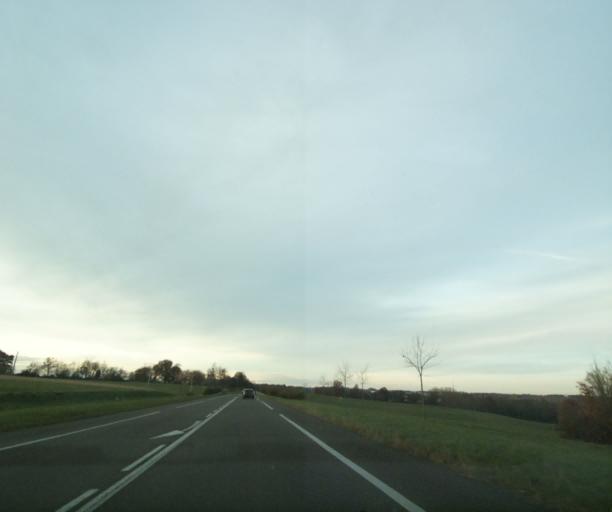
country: FR
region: Aquitaine
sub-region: Departement de la Gironde
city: Bazas
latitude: 44.4214
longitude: -0.2232
